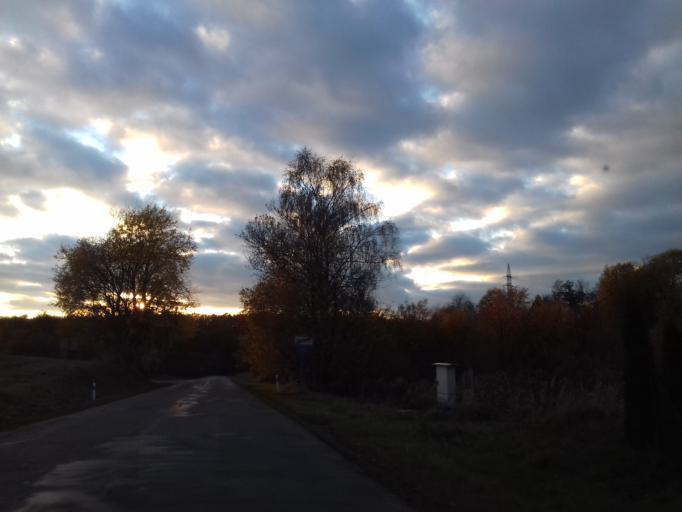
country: CZ
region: Pardubicky
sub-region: Okres Chrudim
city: Skutec
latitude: 49.8331
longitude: 15.9835
